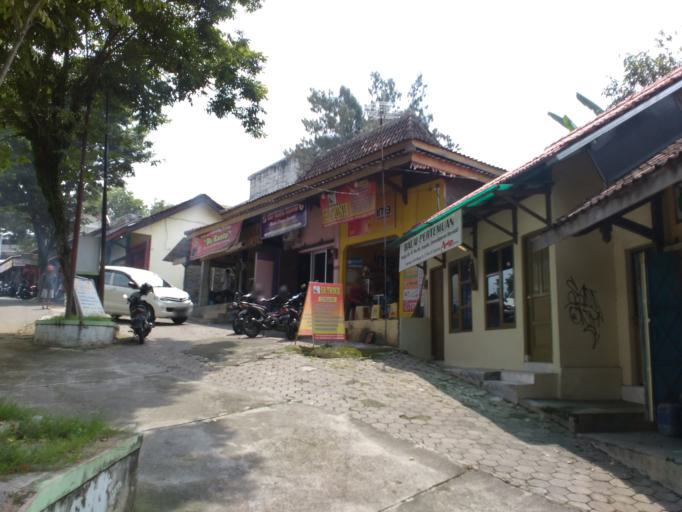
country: ID
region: Central Java
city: Boyolali
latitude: -7.5359
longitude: 110.6017
